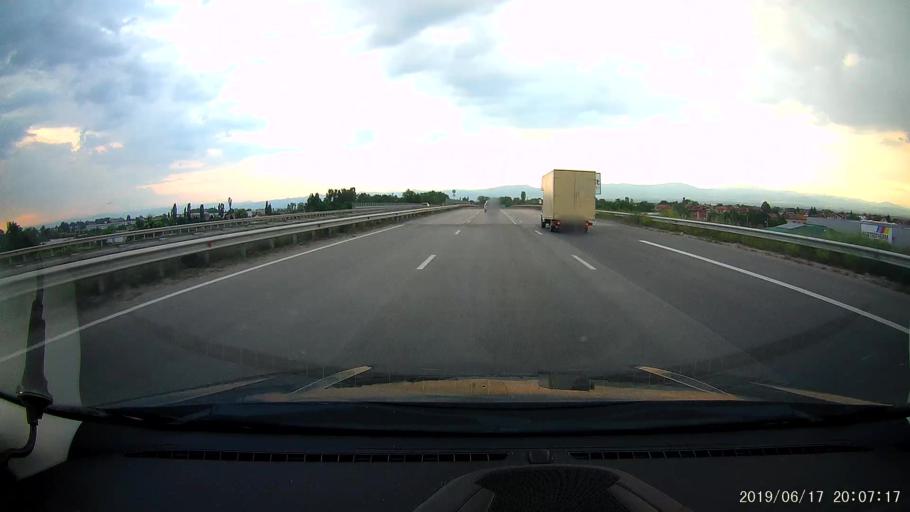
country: BG
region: Sofia-Capital
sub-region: Stolichna Obshtina
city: Sofia
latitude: 42.6537
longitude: 23.4546
